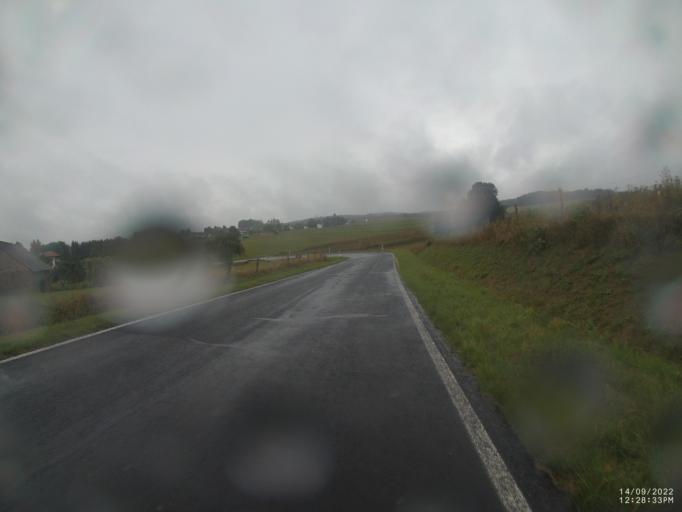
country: DE
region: Rheinland-Pfalz
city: Uxheim
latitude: 50.3471
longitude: 6.7409
